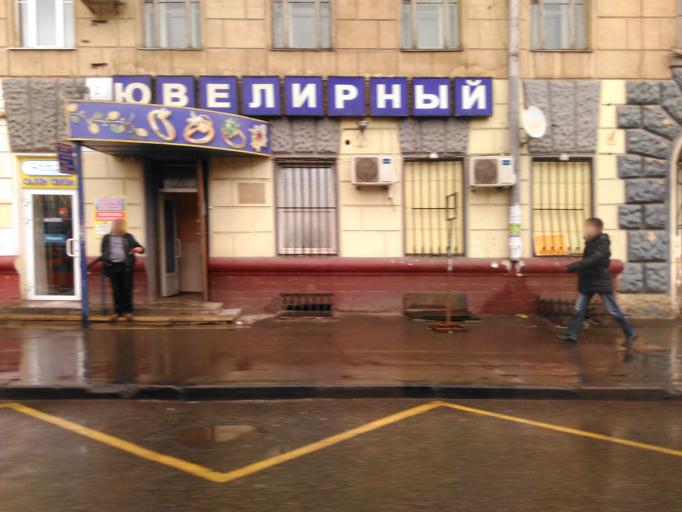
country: RU
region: Moscow
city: Zamoskvorech'ye
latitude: 55.7304
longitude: 37.6430
